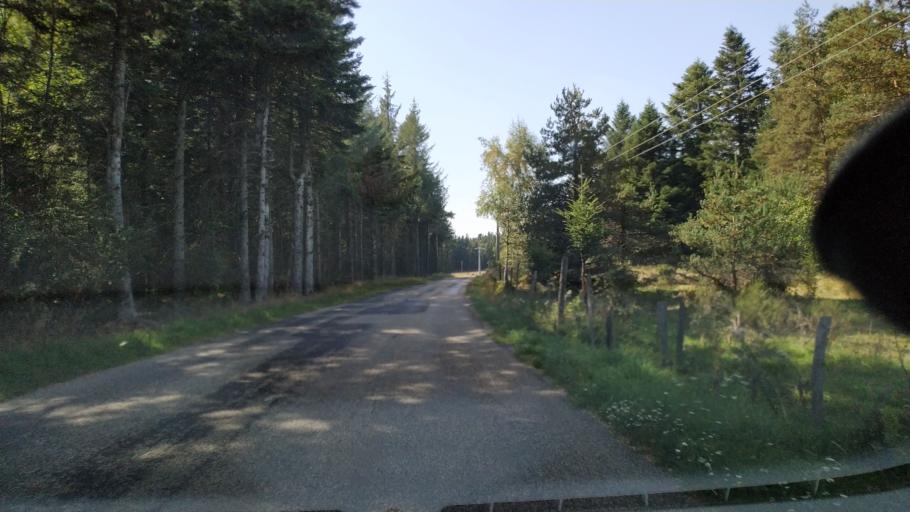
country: FR
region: Rhone-Alpes
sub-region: Departement de l'Ardeche
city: Saint-Agreve
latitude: 45.0225
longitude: 4.4176
